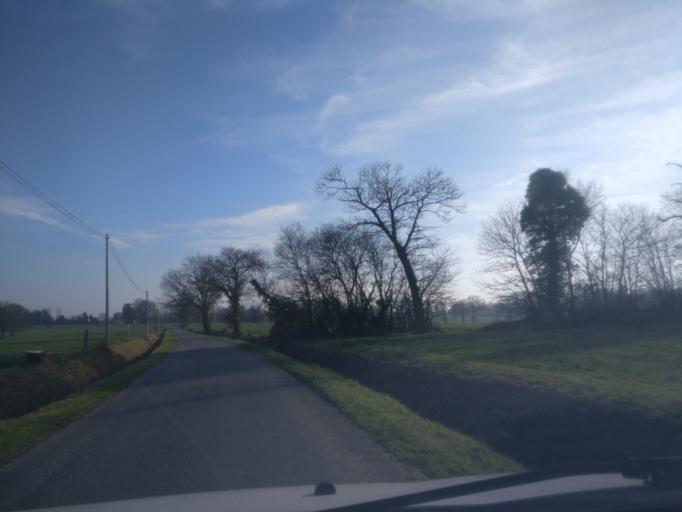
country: FR
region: Brittany
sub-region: Departement d'Ille-et-Vilaine
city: Montreuil-sous-Perouse
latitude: 48.2015
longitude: -1.2804
